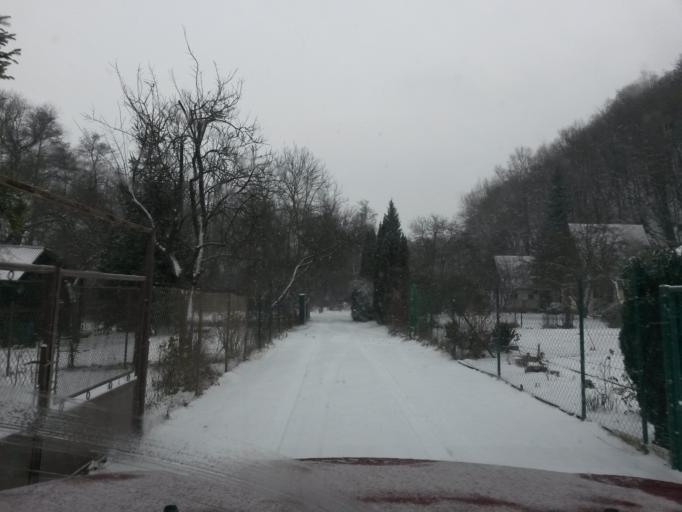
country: SK
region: Kosicky
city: Kosice
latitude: 48.7842
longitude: 21.2477
